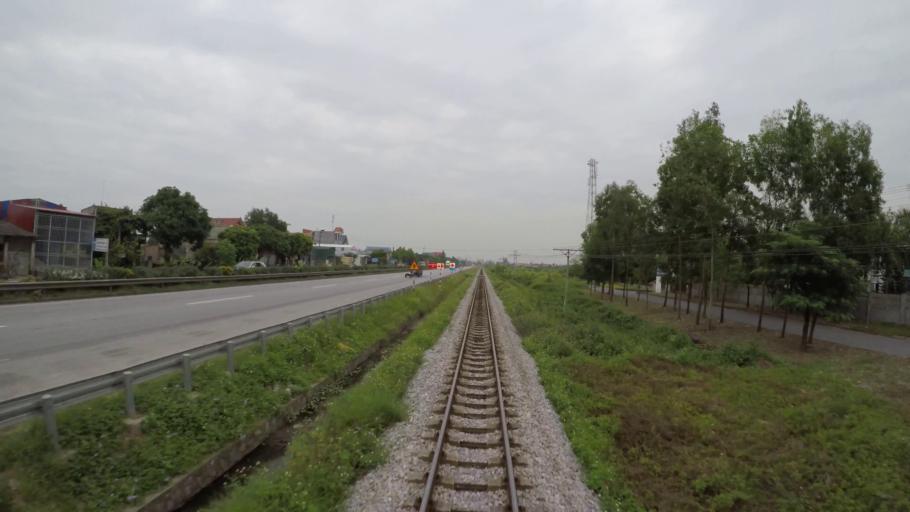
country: VN
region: Hai Duong
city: Phu Thai
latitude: 20.9688
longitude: 106.4513
